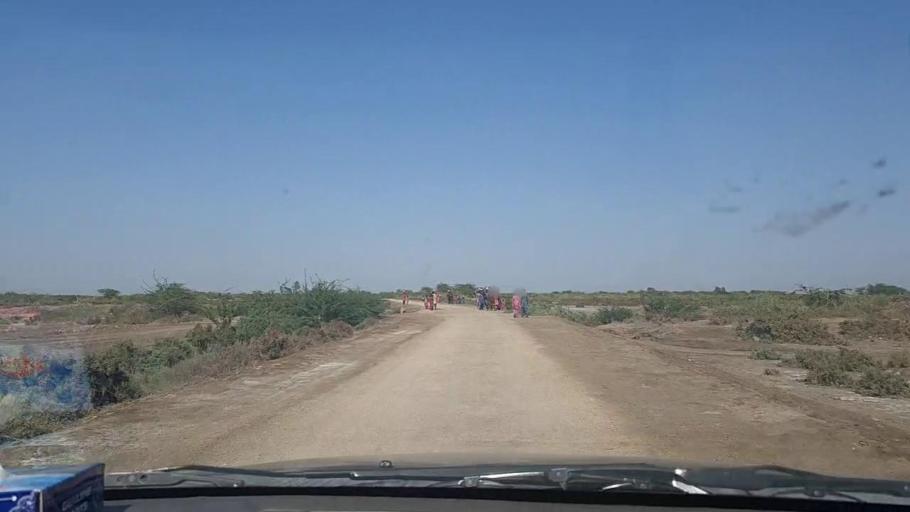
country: PK
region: Sindh
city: Chuhar Jamali
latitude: 24.2756
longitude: 67.7609
